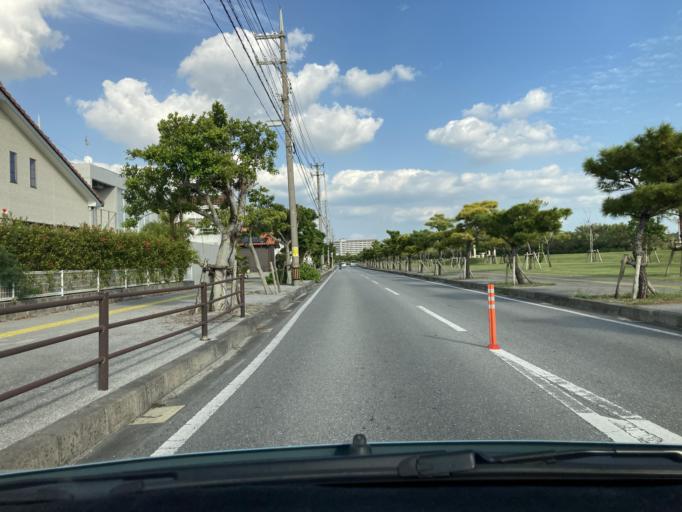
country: JP
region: Okinawa
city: Itoman
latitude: 26.1530
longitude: 127.6640
